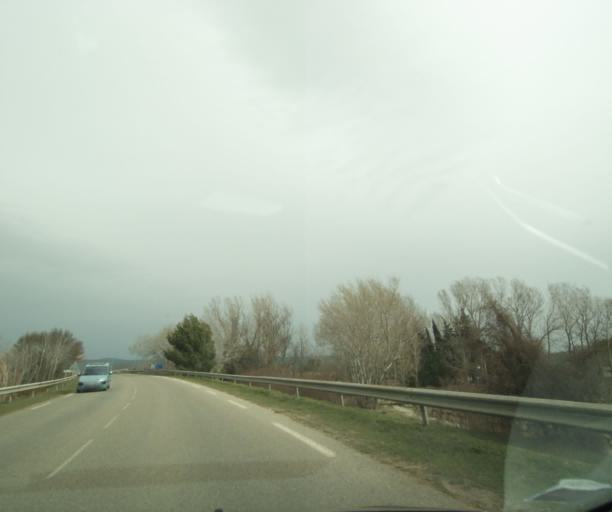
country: FR
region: Provence-Alpes-Cote d'Azur
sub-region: Departement du Var
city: Pourrieres
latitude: 43.4763
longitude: 5.7154
